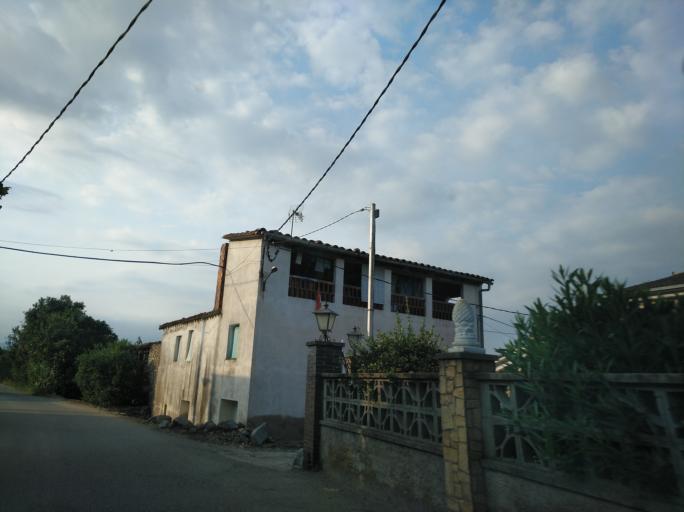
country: ES
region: Catalonia
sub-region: Provincia de Girona
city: la Cellera de Ter
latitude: 41.9612
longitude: 2.6229
